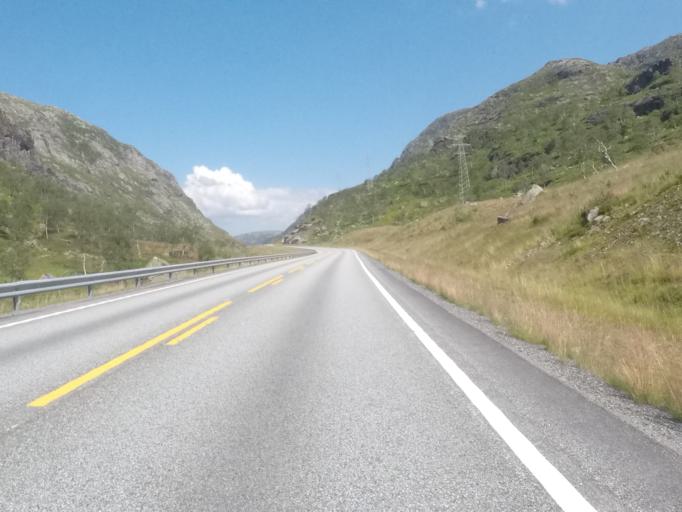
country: NO
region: Hordaland
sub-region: Modalen
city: Mo
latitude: 60.8047
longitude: 5.6172
